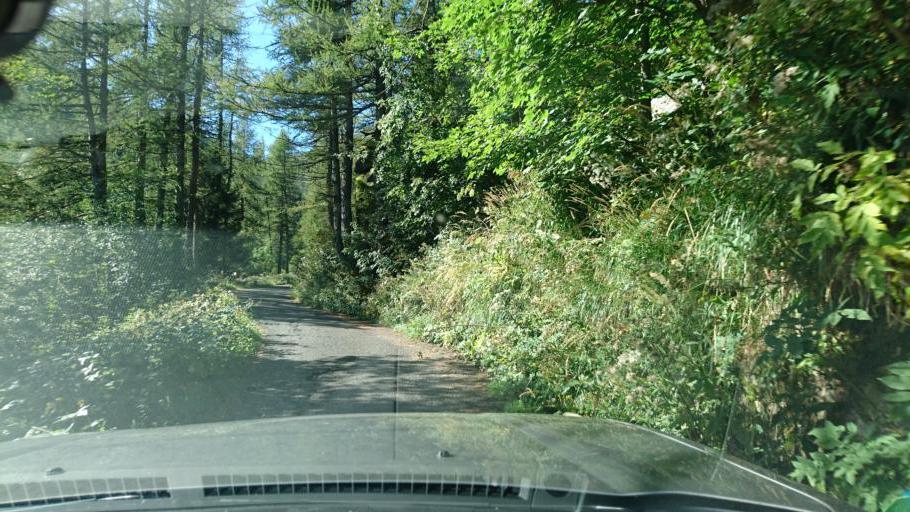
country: IT
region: Lombardy
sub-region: Provincia di Brescia
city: Lozio
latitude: 46.0433
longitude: 10.2222
